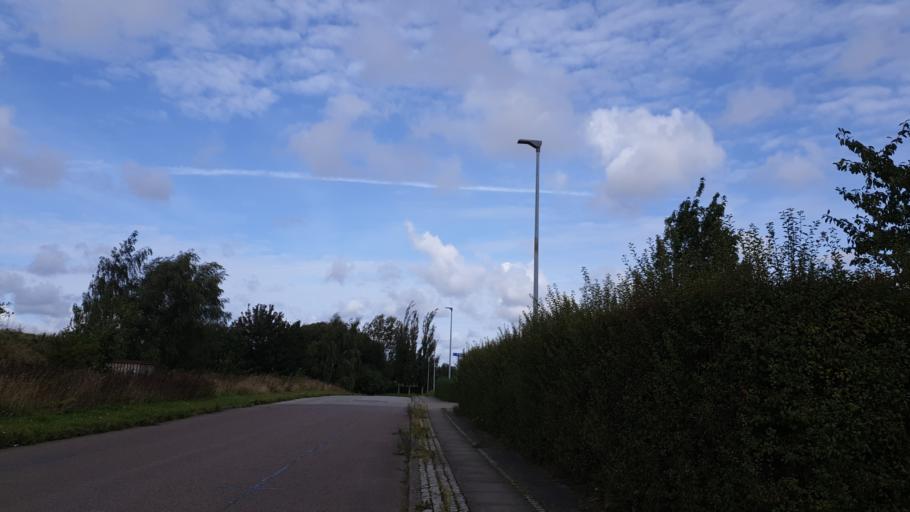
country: DK
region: Central Jutland
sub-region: Hedensted Kommune
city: Hedensted
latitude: 55.8095
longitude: 9.6881
